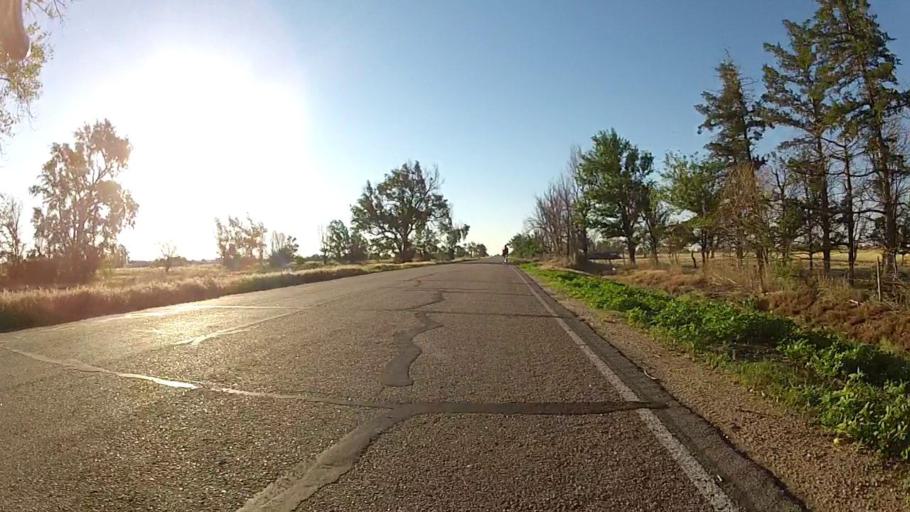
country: US
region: Kansas
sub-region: Ford County
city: Dodge City
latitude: 37.7113
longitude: -99.9206
